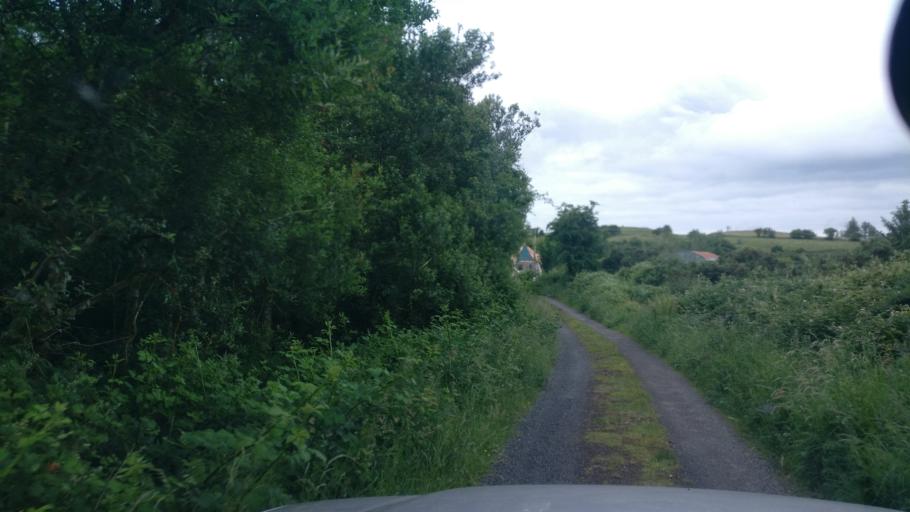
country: IE
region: Connaught
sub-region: County Galway
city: Loughrea
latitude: 53.1469
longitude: -8.5584
